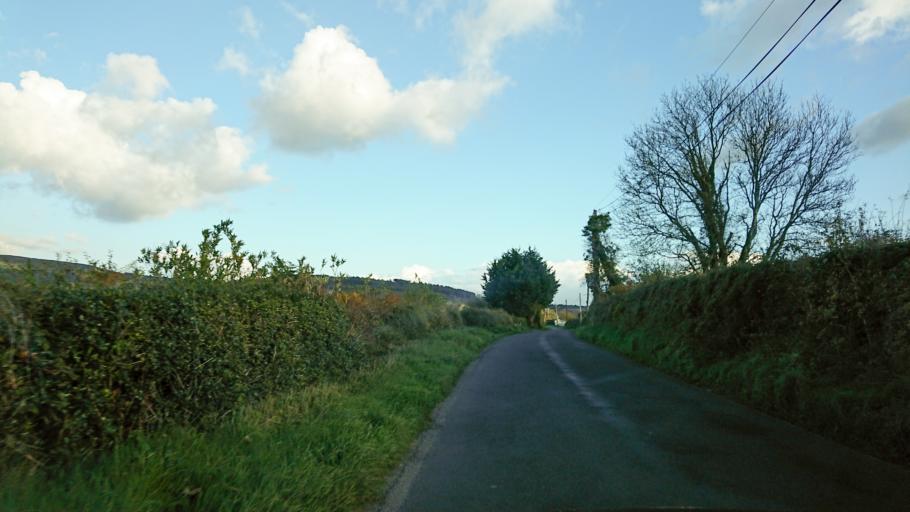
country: IE
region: Leinster
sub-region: Kilkenny
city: Graiguenamanagh
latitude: 52.4742
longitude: -6.9088
